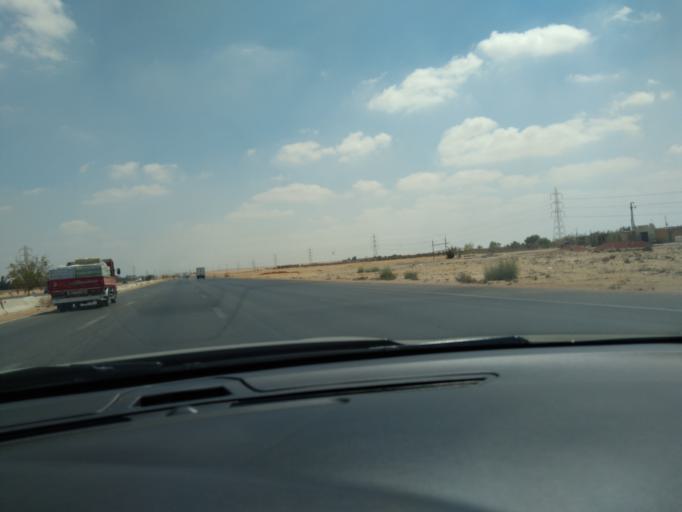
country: EG
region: Al Isma'iliyah
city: At Tall al Kabir
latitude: 30.3549
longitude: 31.8933
